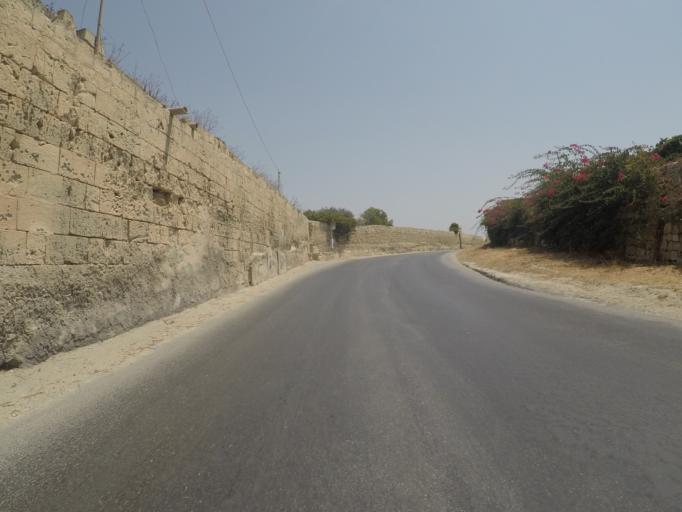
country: MT
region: Is-Siggiewi
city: Siggiewi
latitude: 35.8567
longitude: 14.4218
